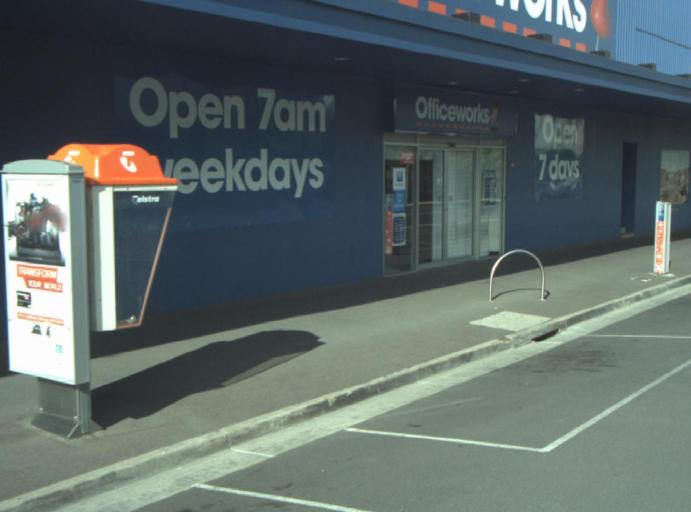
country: AU
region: Victoria
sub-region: Greater Geelong
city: Geelong
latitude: -38.1483
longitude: 144.3643
